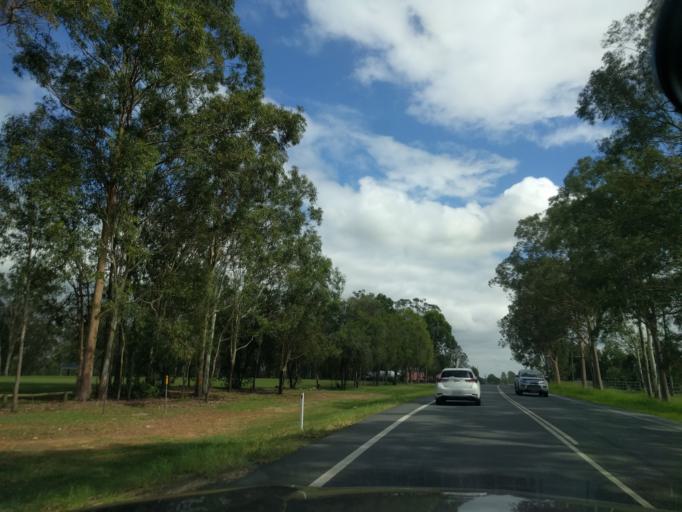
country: AU
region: Queensland
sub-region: Logan
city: Cedar Vale
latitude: -27.9019
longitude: 152.9751
